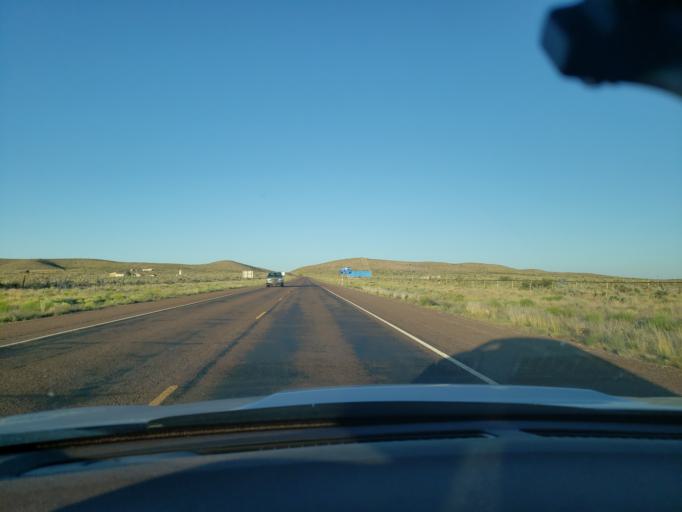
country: US
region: Texas
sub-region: El Paso County
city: Homestead Meadows South
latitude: 31.8267
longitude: -105.9088
